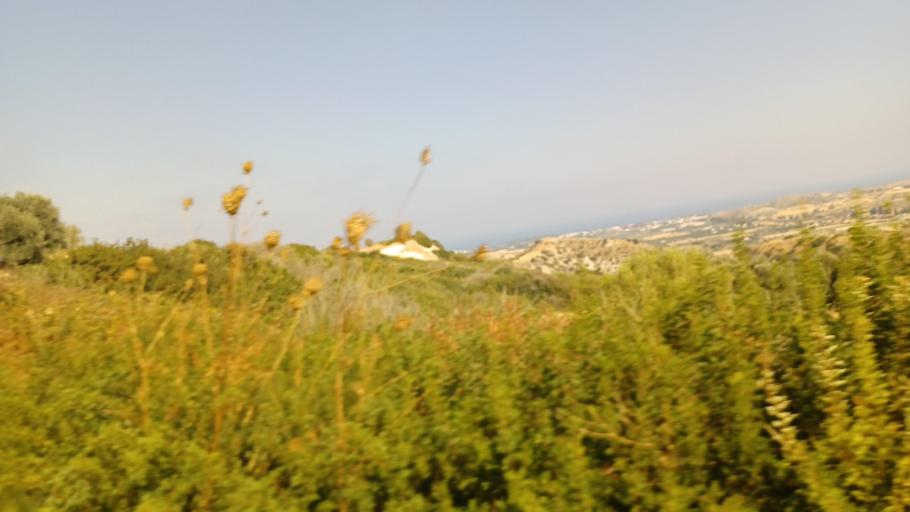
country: CY
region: Pafos
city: Polis
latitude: 34.9904
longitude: 32.4307
